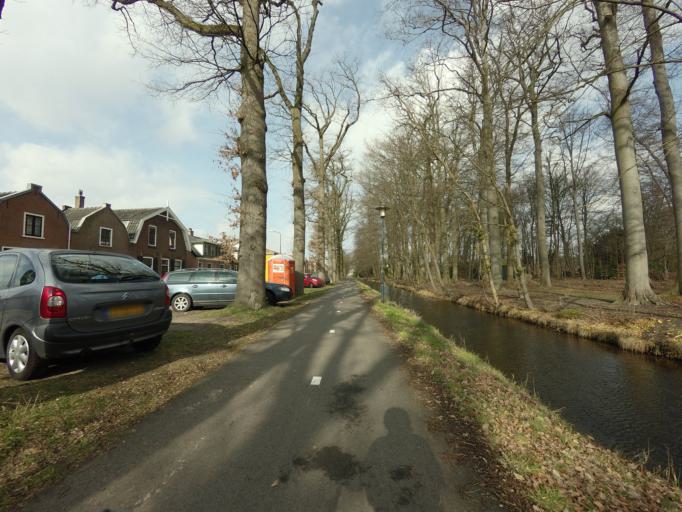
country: NL
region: North Holland
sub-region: Gemeente Wijdemeren
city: Kortenhoef
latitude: 52.2342
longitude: 5.1220
